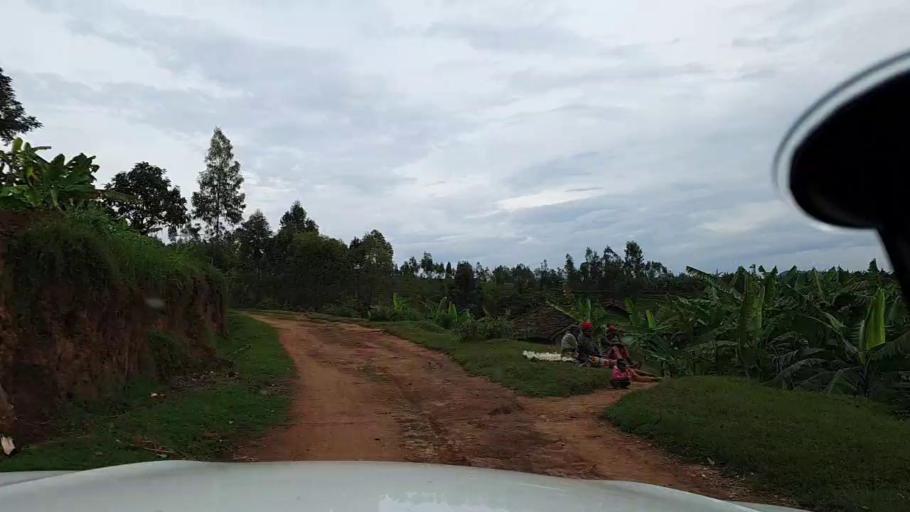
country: RW
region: Southern Province
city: Gitarama
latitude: -2.1209
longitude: 29.6484
